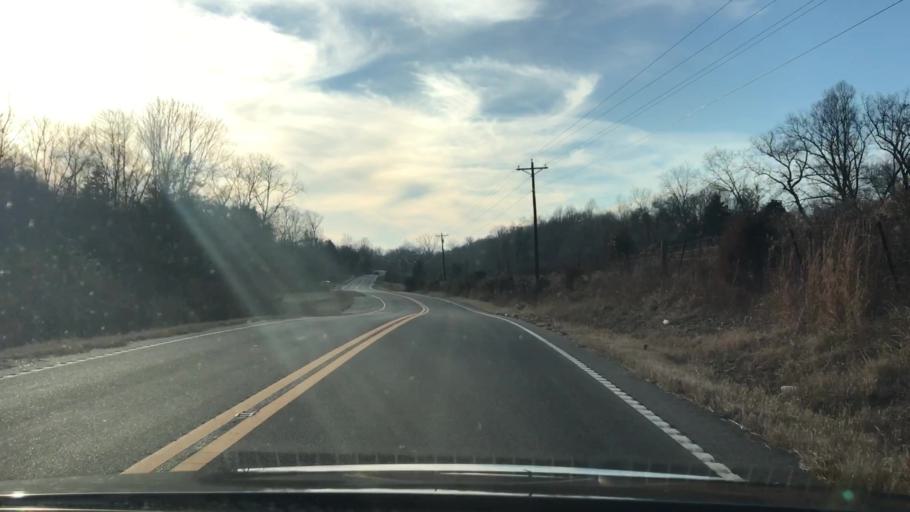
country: US
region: Tennessee
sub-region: Macon County
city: Red Boiling Springs
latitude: 36.6173
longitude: -85.7959
